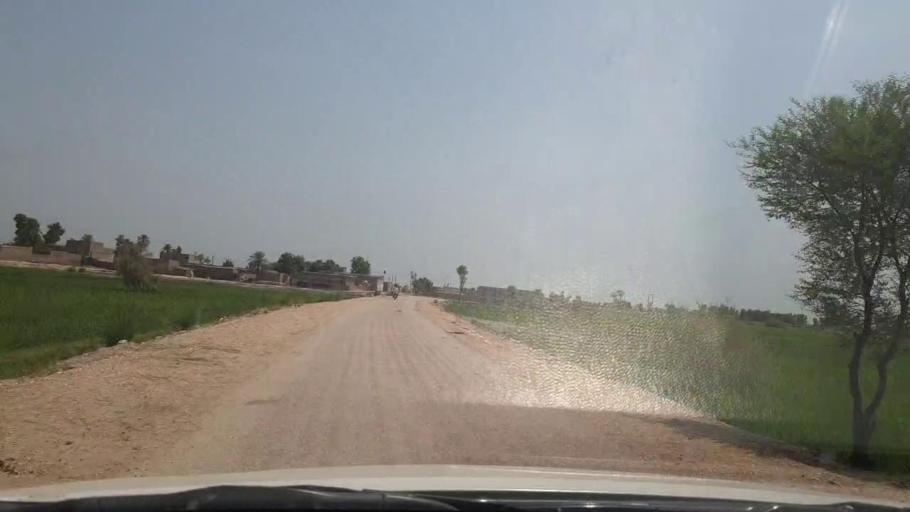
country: PK
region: Sindh
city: Rustam jo Goth
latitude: 28.0269
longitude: 68.7993
